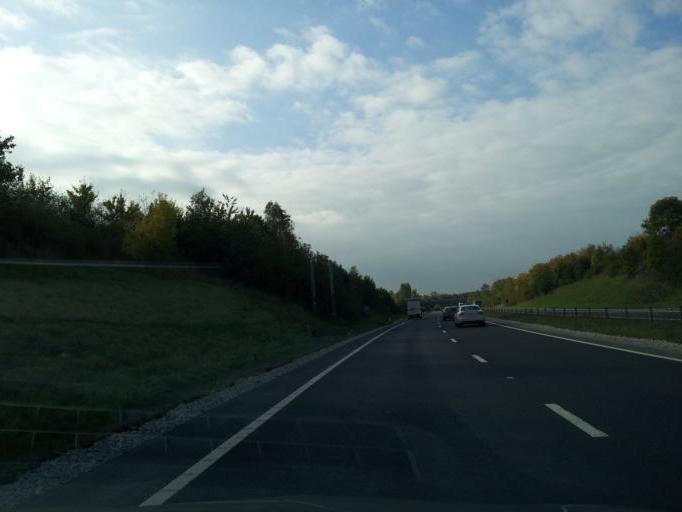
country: GB
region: England
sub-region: Northamptonshire
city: Silverstone
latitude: 52.0896
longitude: -1.0166
